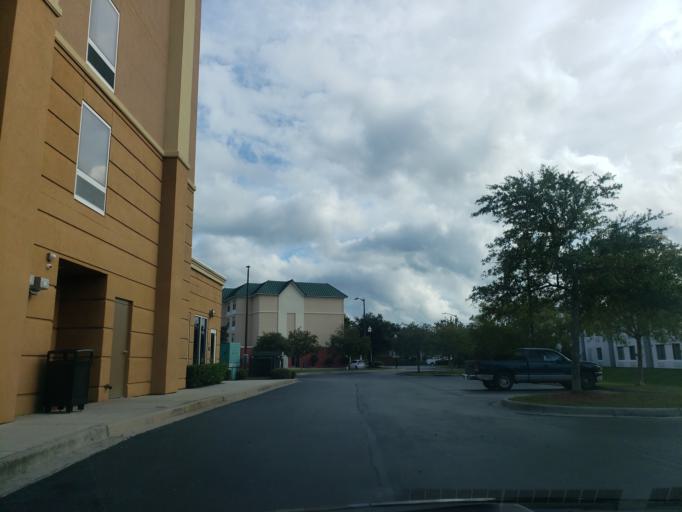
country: US
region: Georgia
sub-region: Chatham County
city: Georgetown
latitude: 32.0058
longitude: -81.2768
